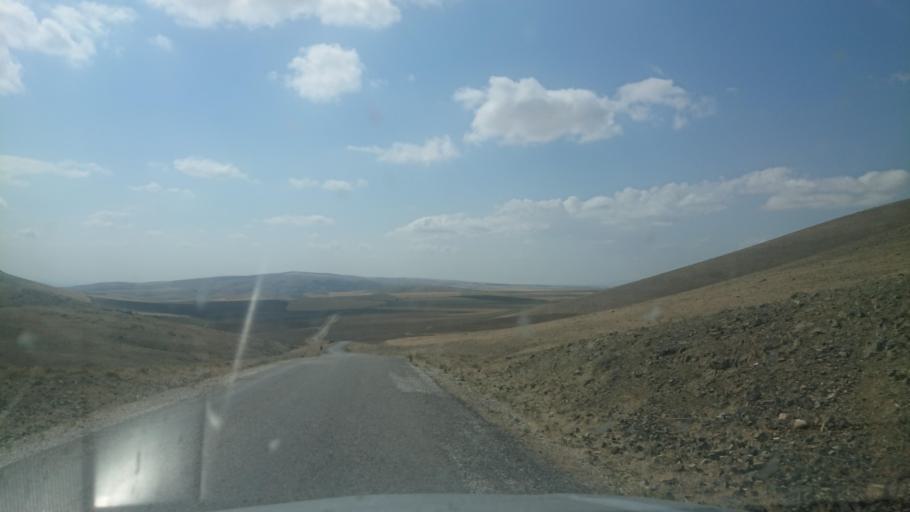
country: TR
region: Aksaray
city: Sariyahsi
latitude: 39.0019
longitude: 33.9727
